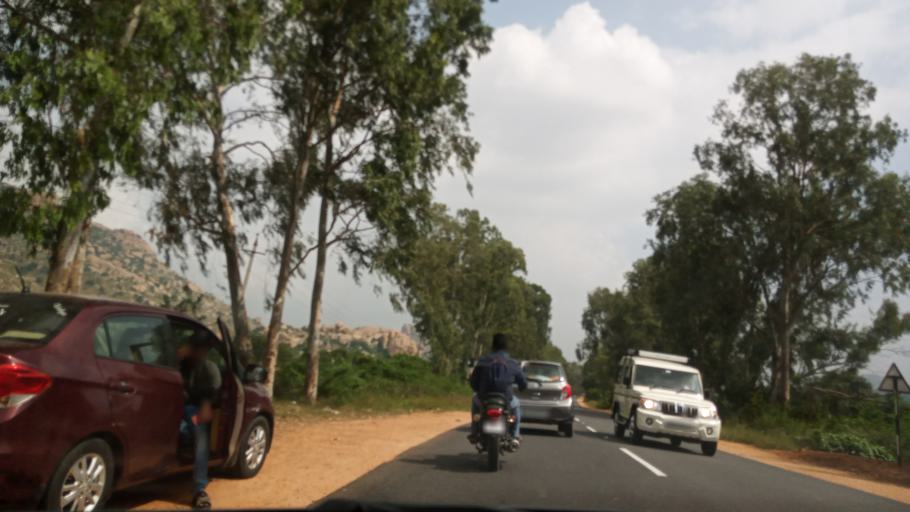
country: IN
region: Andhra Pradesh
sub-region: Chittoor
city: Madanapalle
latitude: 13.6359
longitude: 78.6019
